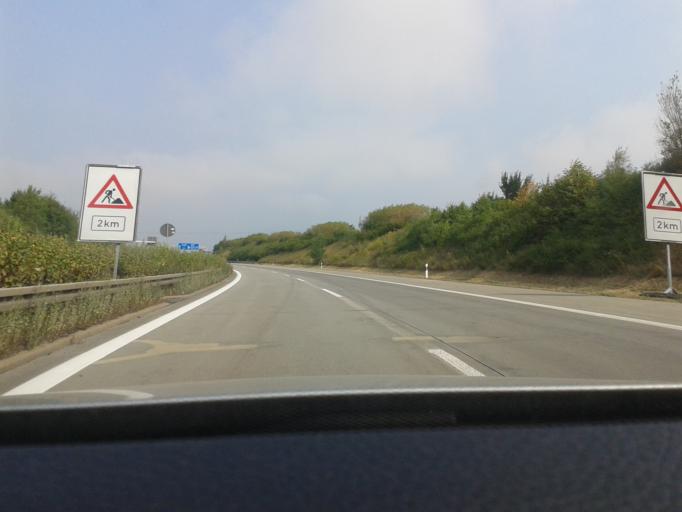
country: DE
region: Saxony
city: Freital
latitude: 51.0475
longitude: 13.6075
